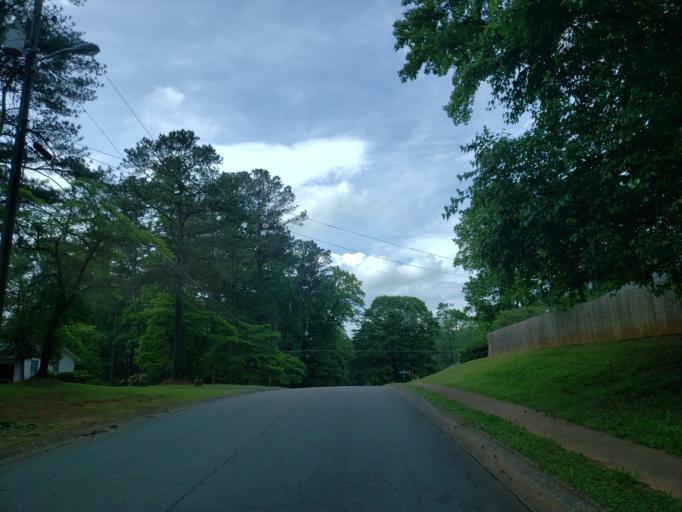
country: US
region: Georgia
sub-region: Cobb County
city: Marietta
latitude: 33.9598
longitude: -84.5688
